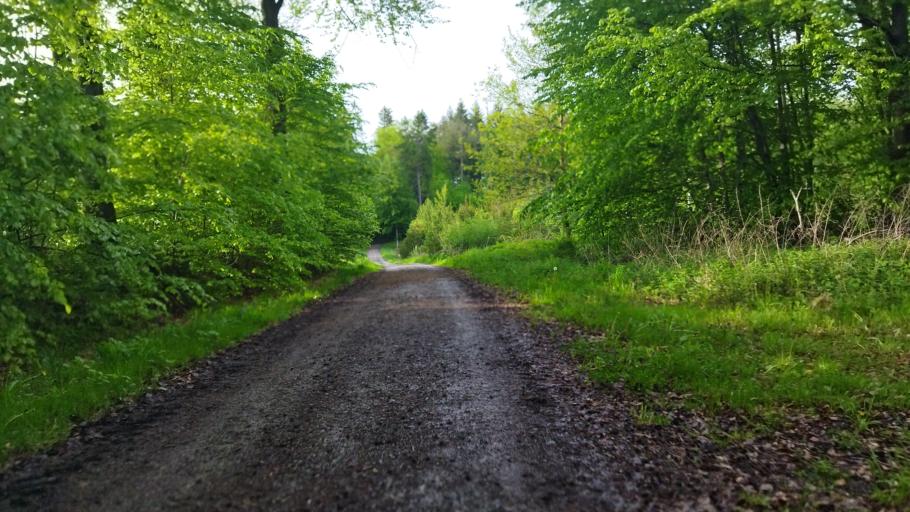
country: DE
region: Baden-Wuerttemberg
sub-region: Regierungsbezirk Stuttgart
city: Mundelsheim
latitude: 49.0233
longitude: 9.2269
